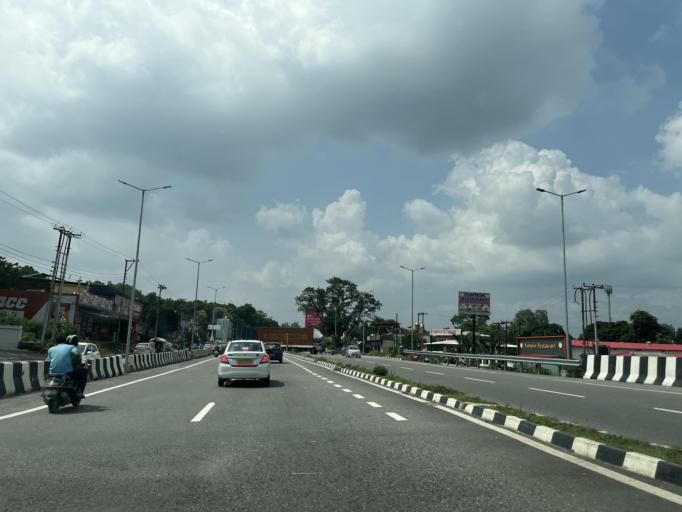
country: IN
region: Uttarakhand
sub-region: Dehradun
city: Raipur
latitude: 30.2458
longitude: 78.0980
